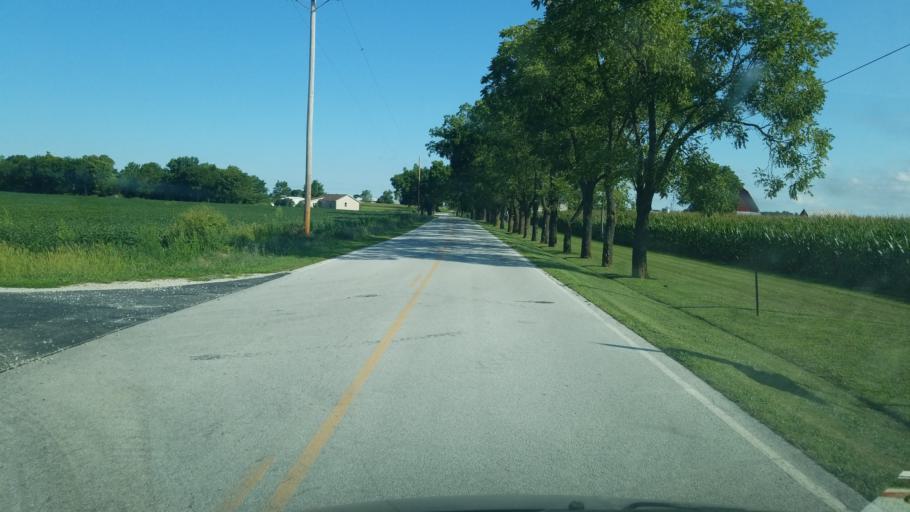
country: US
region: Ohio
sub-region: Wyandot County
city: Carey
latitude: 40.9847
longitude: -83.3676
